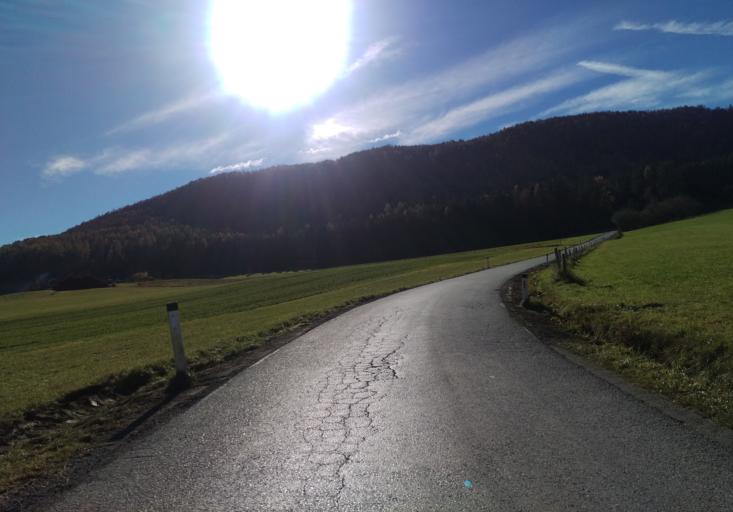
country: AT
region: Styria
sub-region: Politischer Bezirk Graz-Umgebung
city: Sankt Radegund bei Graz
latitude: 47.1329
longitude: 15.4863
